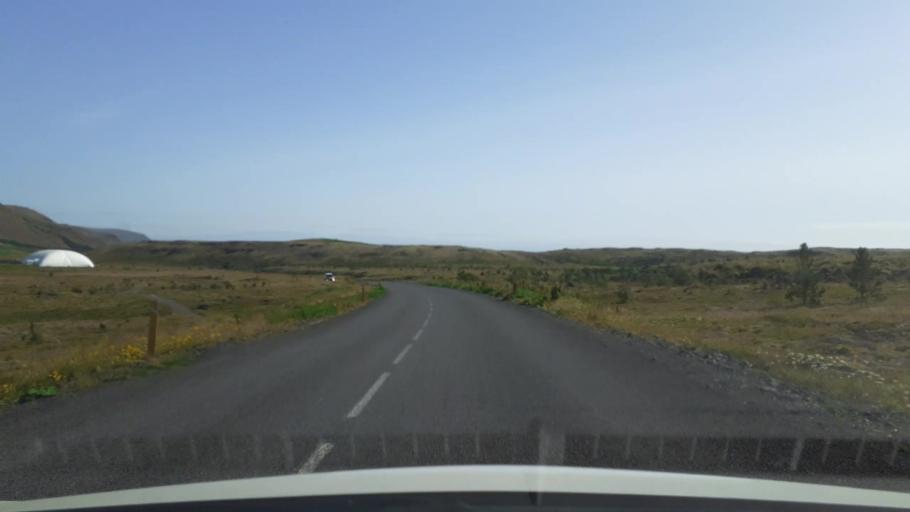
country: IS
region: South
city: Hveragerdi
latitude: 64.0155
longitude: -21.2101
